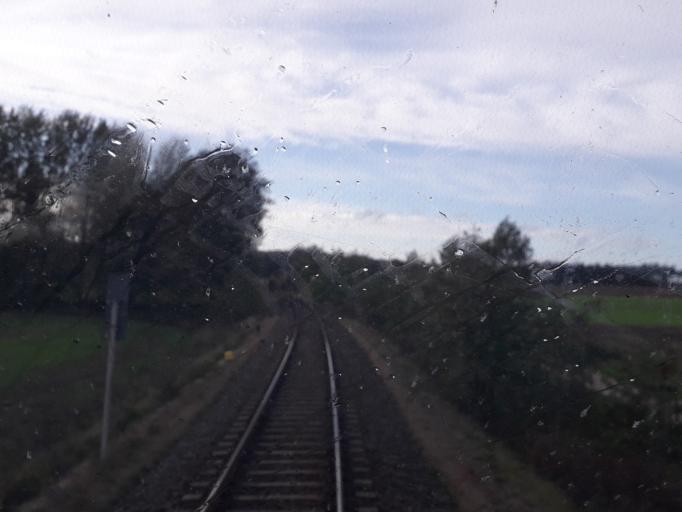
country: DE
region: Brandenburg
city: Heiligengrabe
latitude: 53.1533
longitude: 12.3699
